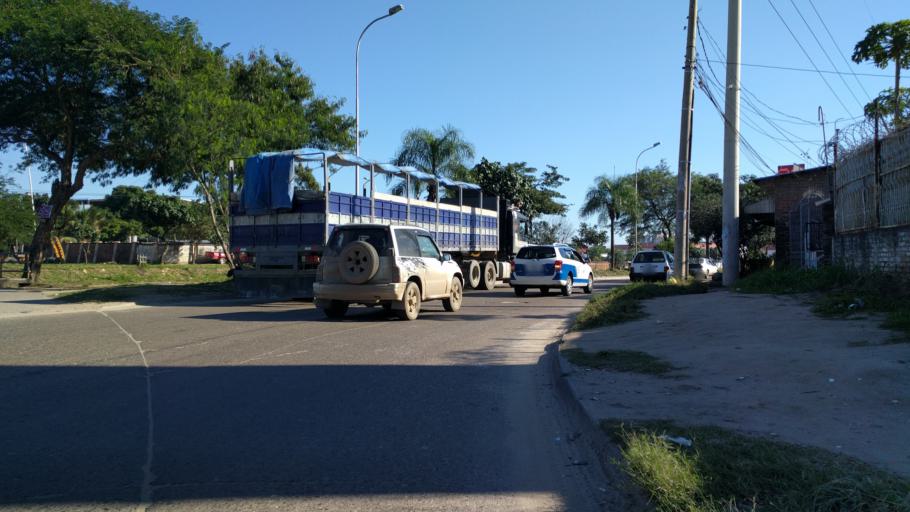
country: BO
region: Santa Cruz
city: Santa Cruz de la Sierra
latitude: -17.7914
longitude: -63.2164
